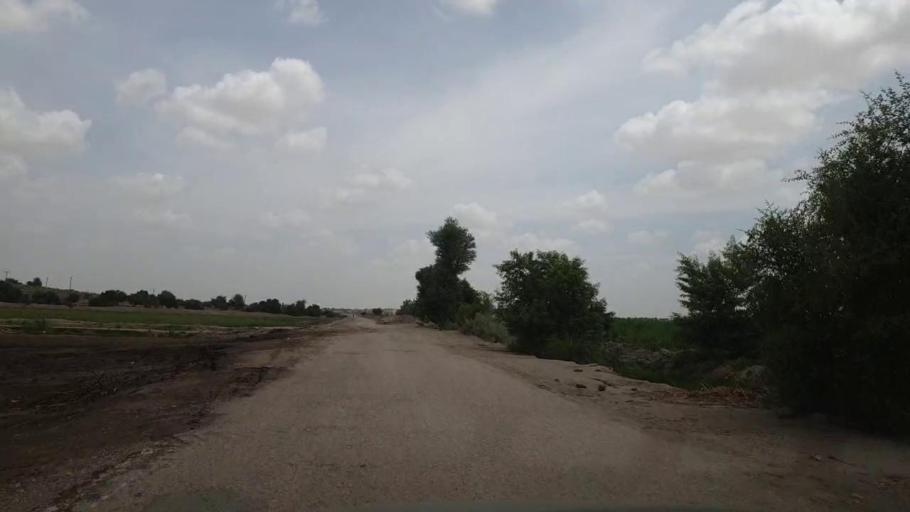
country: PK
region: Sindh
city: Kot Diji
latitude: 27.2041
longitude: 69.1198
